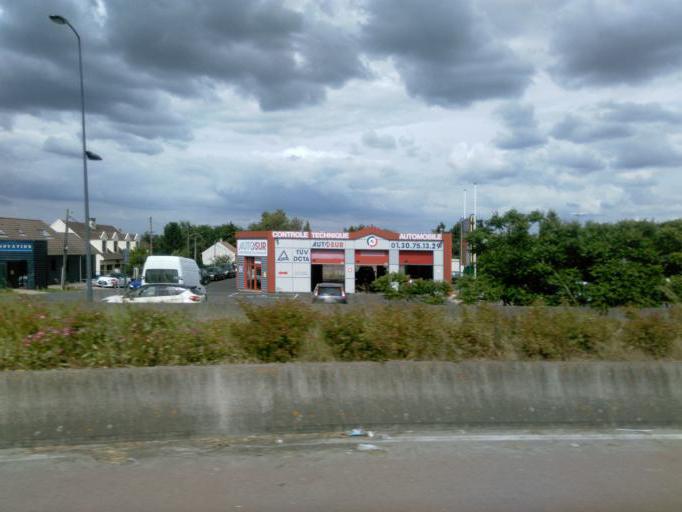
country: FR
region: Ile-de-France
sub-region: Departement du Val-d'Oise
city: Osny
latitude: 49.0733
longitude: 2.0791
